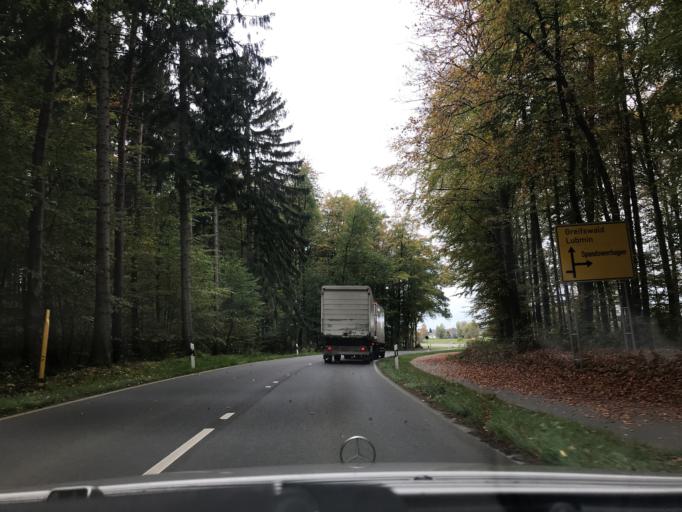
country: DE
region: Mecklenburg-Vorpommern
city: Kroslin
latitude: 54.1401
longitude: 13.7032
